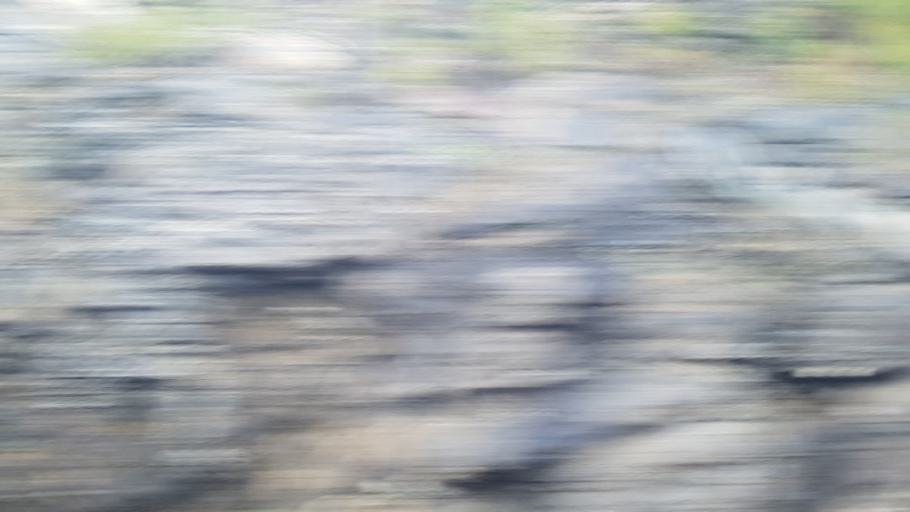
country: NO
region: Sor-Trondelag
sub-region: Rennebu
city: Berkak
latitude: 62.9121
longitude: 10.1335
